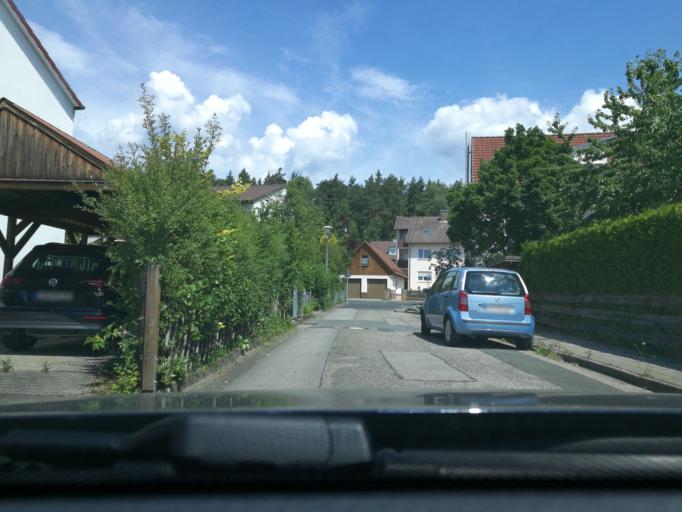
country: DE
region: Bavaria
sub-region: Regierungsbezirk Mittelfranken
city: Schwarzenbruck
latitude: 49.3571
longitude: 11.2355
